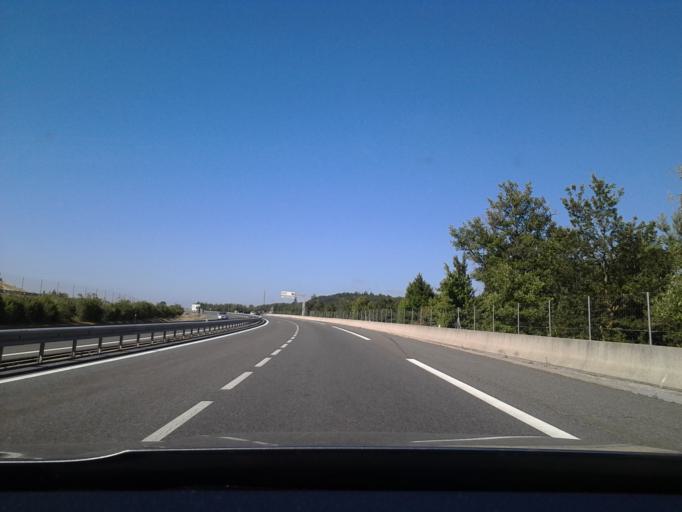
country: FR
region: Midi-Pyrenees
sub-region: Departement de l'Aveyron
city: Severac-le-Chateau
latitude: 44.2599
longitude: 3.0630
